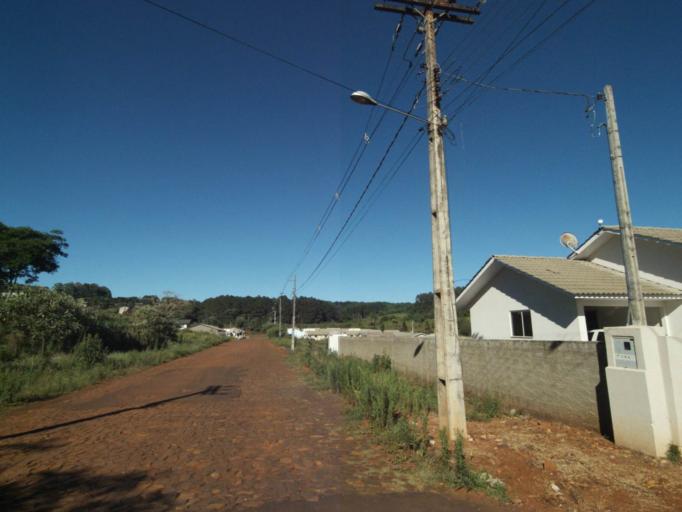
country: BR
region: Santa Catarina
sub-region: Sao Lourenco Do Oeste
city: Sao Lourenco dOeste
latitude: -26.2658
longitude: -52.7850
